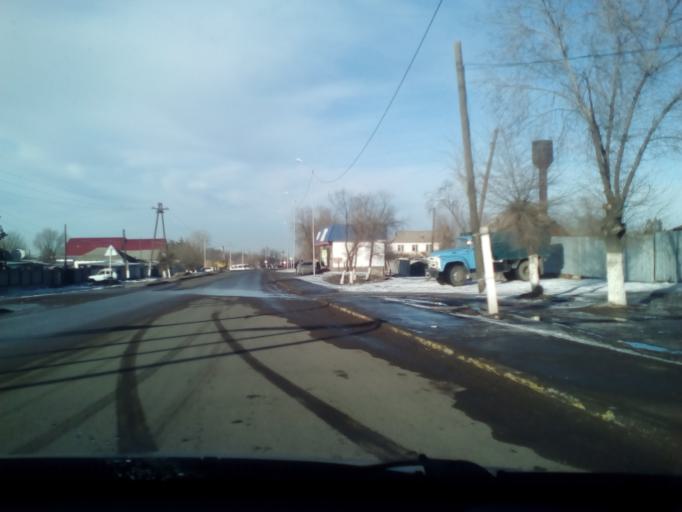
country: KZ
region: Almaty Oblysy
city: Burunday
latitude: 43.1794
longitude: 76.4143
